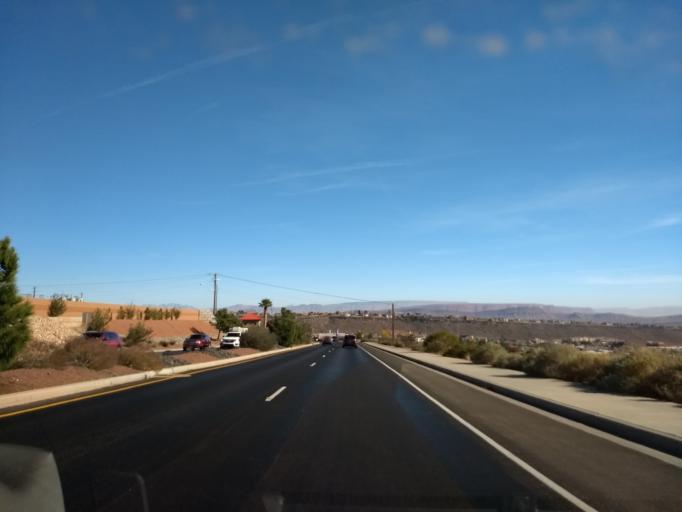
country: US
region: Utah
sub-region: Washington County
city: Saint George
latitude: 37.1124
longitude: -113.5685
